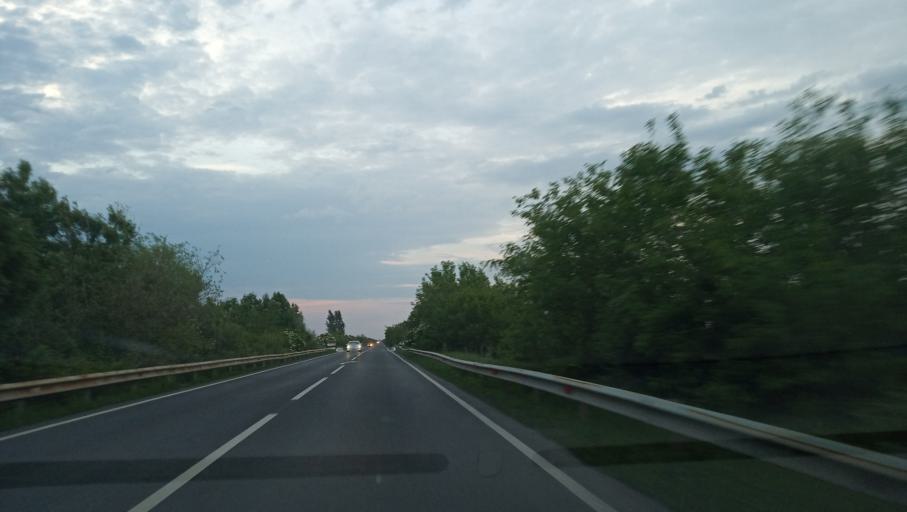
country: RO
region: Timis
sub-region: Comuna Jebel
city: Jebel
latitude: 45.5198
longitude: 21.2336
